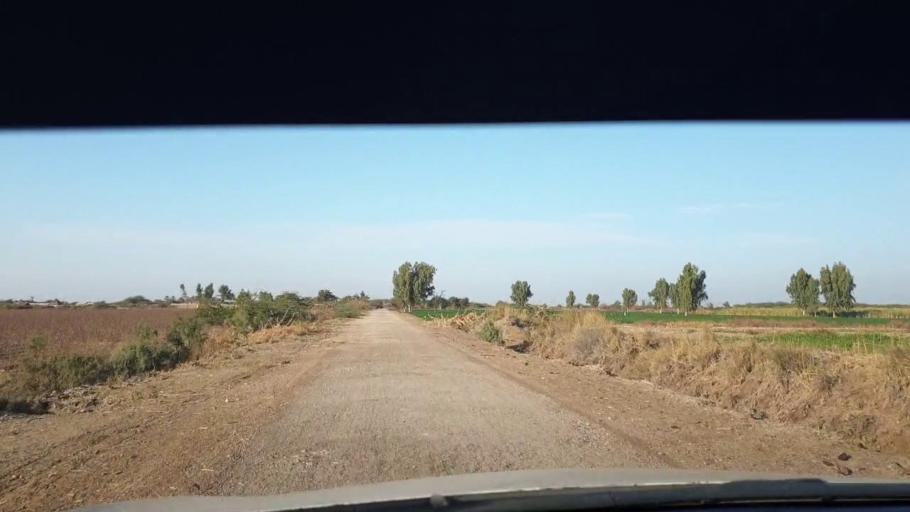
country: PK
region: Sindh
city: Berani
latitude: 25.8191
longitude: 68.9098
